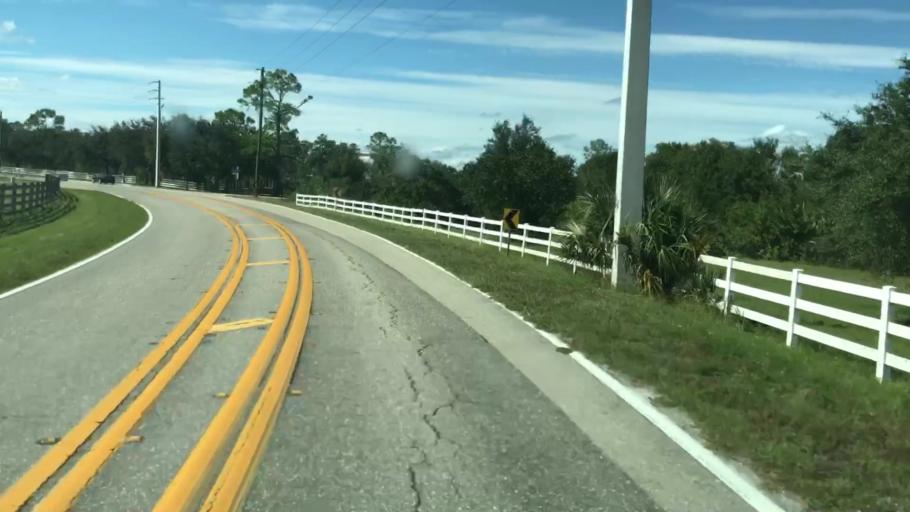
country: US
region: Florida
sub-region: Lee County
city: Olga
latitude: 26.7282
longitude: -81.6835
